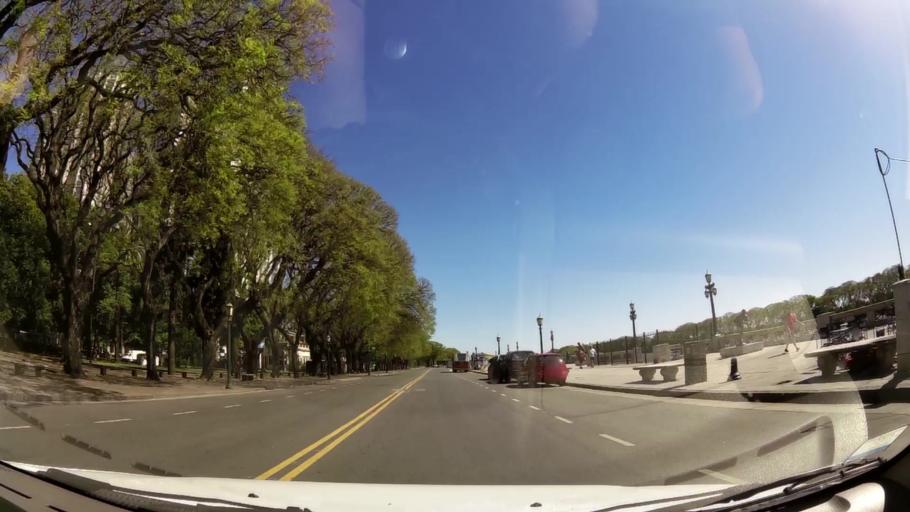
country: AR
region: Buenos Aires F.D.
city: Buenos Aires
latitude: -34.6140
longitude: -58.3577
